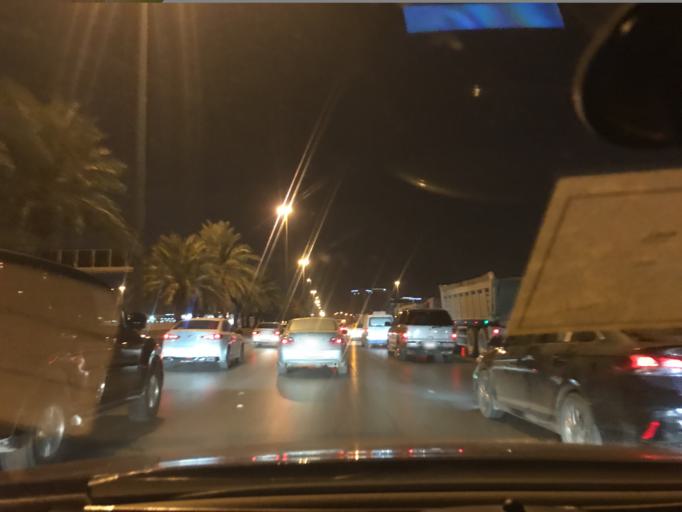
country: SA
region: Ar Riyad
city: Riyadh
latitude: 24.7727
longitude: 46.7325
